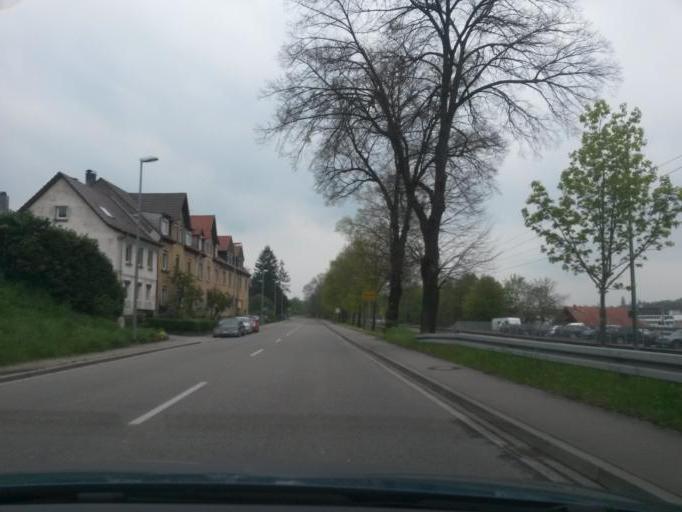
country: DE
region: Baden-Wuerttemberg
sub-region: Karlsruhe Region
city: Birkenfeld
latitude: 48.8844
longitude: 8.6588
